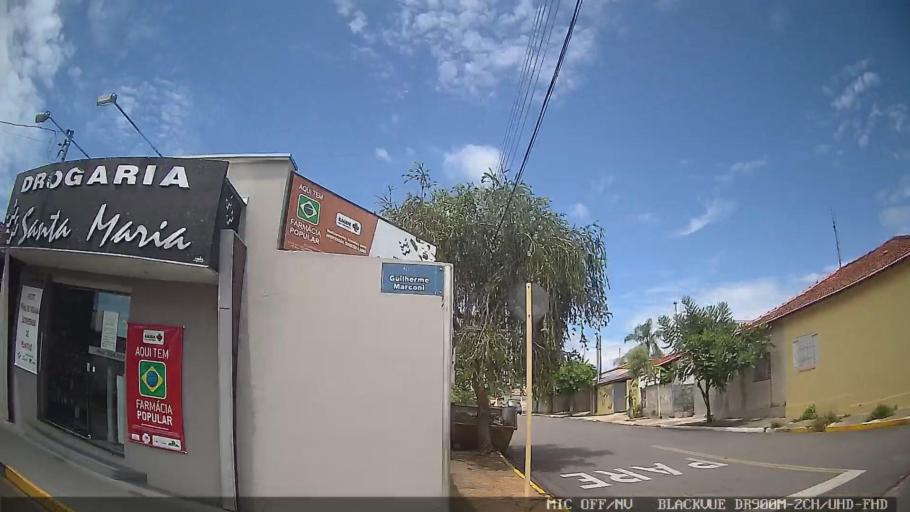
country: BR
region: Sao Paulo
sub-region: Laranjal Paulista
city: Laranjal Paulista
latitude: -23.0577
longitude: -47.8334
